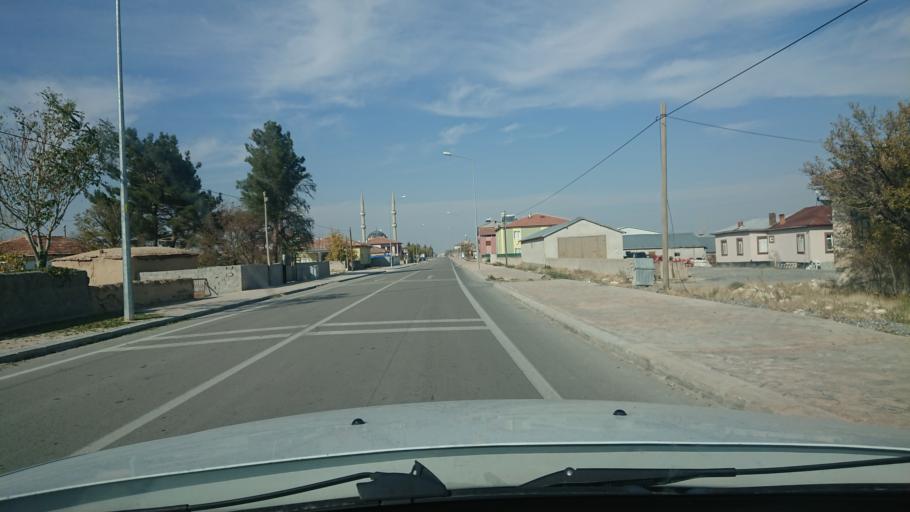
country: TR
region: Aksaray
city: Sultanhani
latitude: 38.2558
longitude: 33.4471
